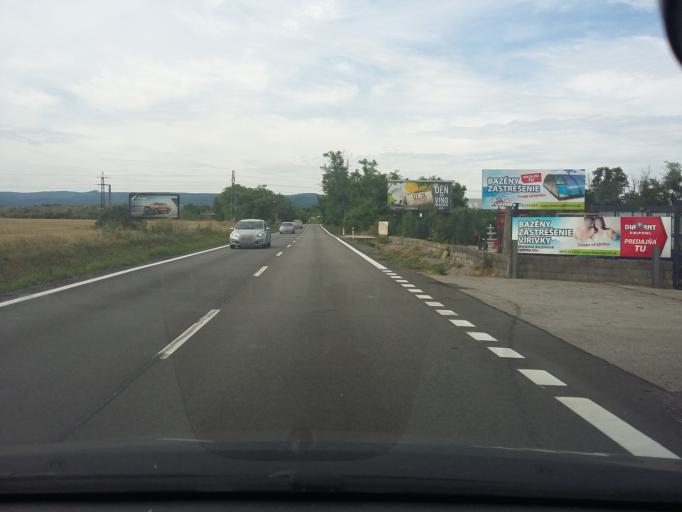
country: SK
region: Bratislavsky
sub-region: Okres Pezinok
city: Pezinok
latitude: 48.2826
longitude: 17.2901
